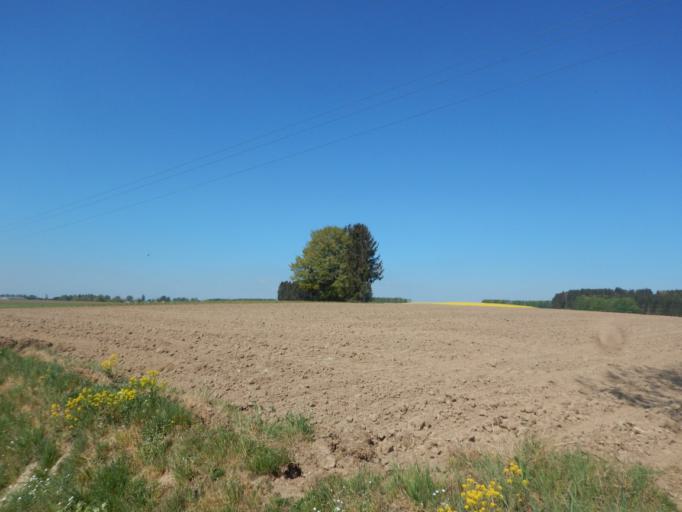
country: LU
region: Diekirch
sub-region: Canton de Clervaux
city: Troisvierges
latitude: 50.1585
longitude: 5.9988
